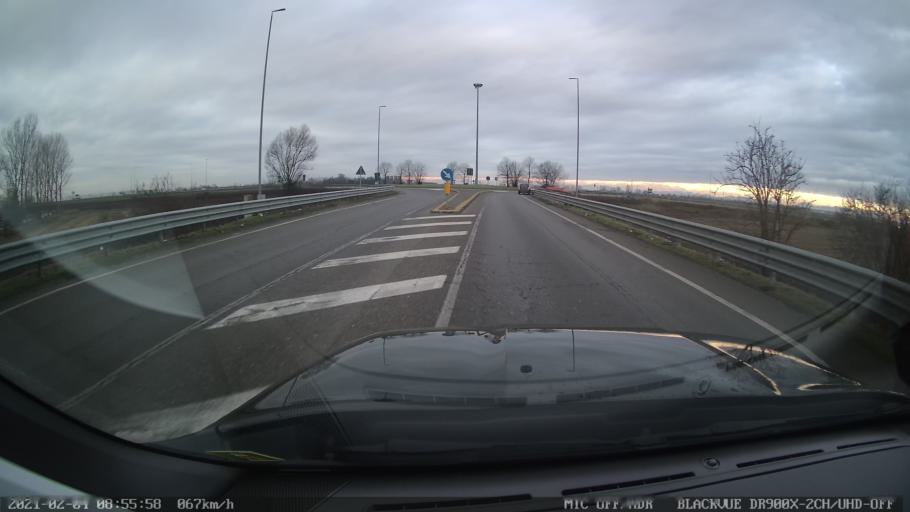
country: IT
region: Piedmont
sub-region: Provincia di Novara
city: San Pietro Mosezzo
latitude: 45.4770
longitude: 8.5588
